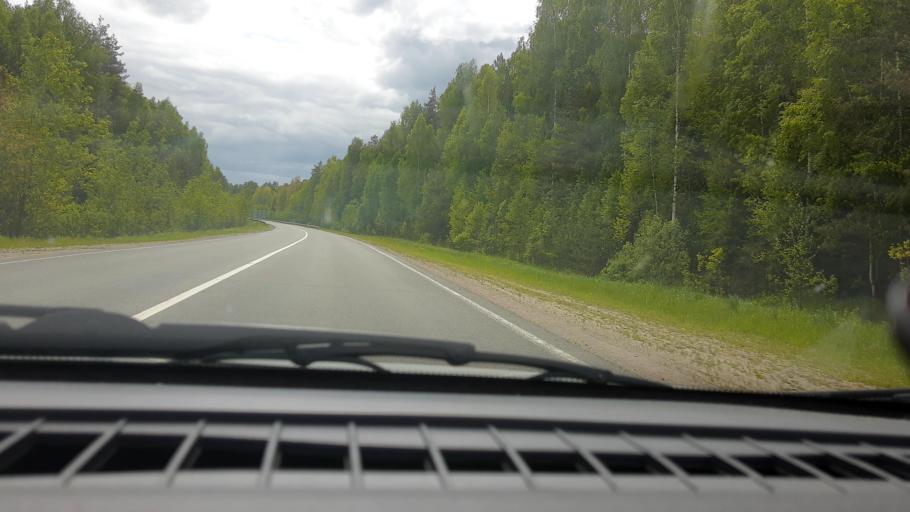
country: RU
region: Nizjnij Novgorod
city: Semenov
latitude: 56.8064
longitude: 44.4636
